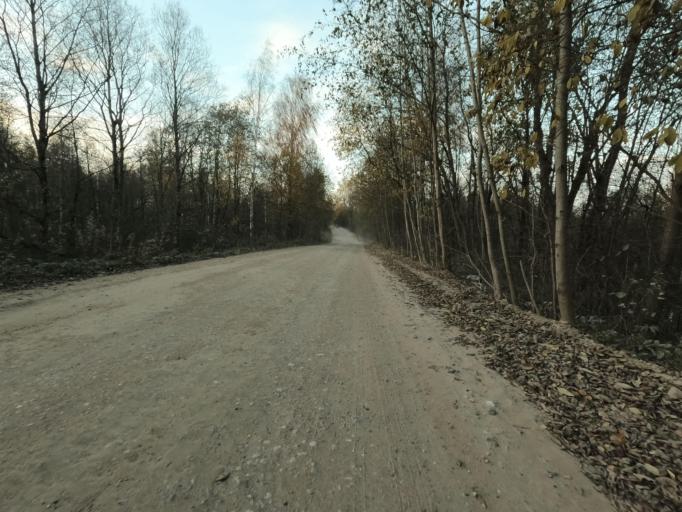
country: RU
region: Leningrad
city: Mga
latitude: 59.7725
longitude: 31.2265
